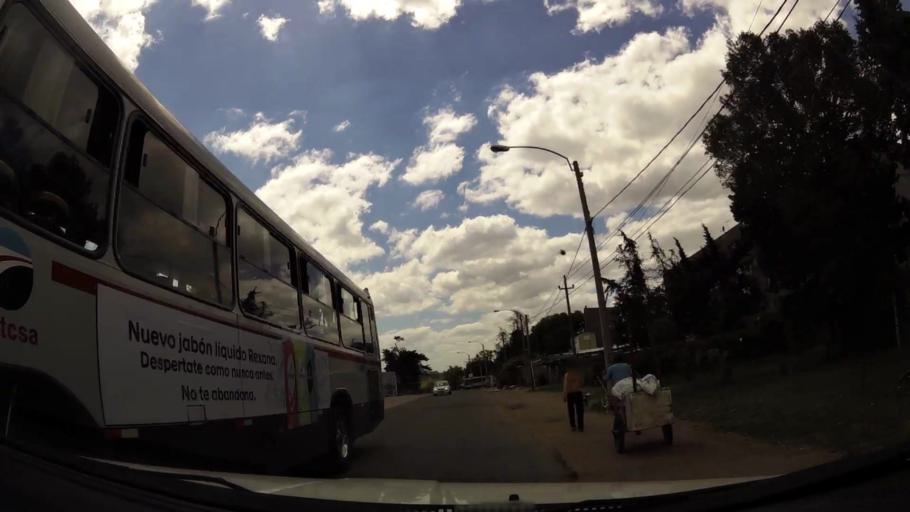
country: UY
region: Canelones
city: La Paz
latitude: -34.8219
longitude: -56.2493
